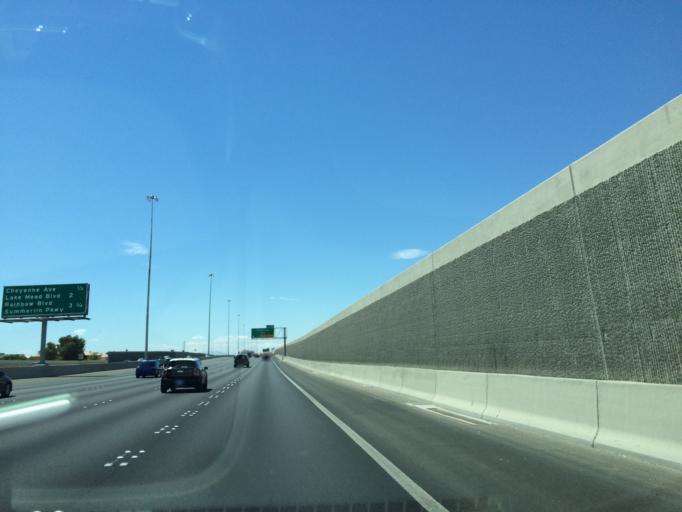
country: US
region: Nevada
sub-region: Clark County
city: Spring Valley
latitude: 36.2296
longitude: -115.2470
